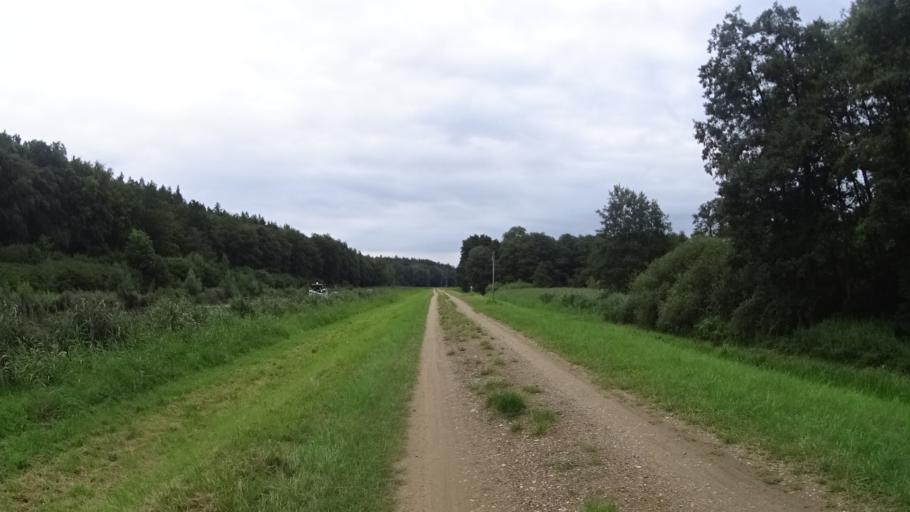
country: DE
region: Schleswig-Holstein
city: Lankau
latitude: 53.6543
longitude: 10.6438
